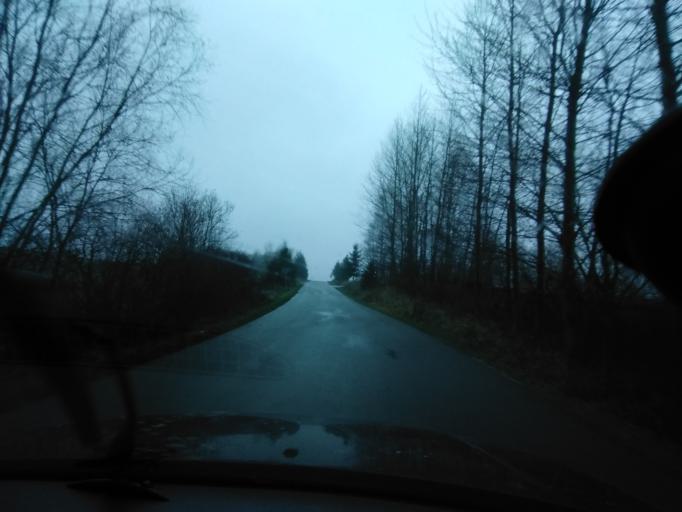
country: PL
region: Subcarpathian Voivodeship
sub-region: Powiat brzozowski
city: Jablonka
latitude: 49.7405
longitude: 22.1098
